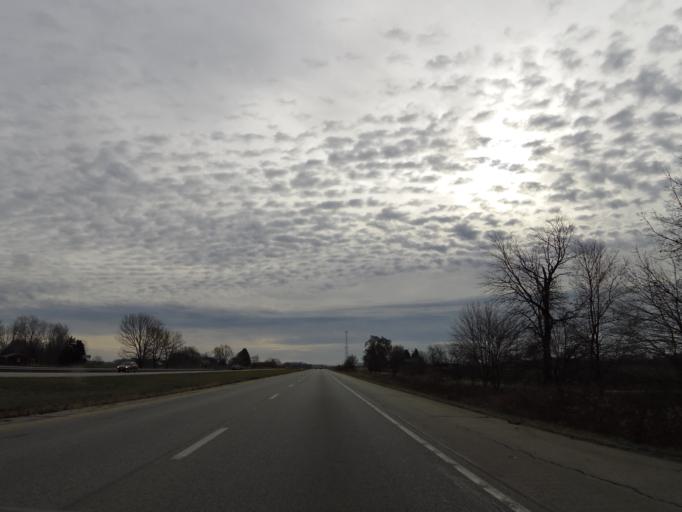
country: US
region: Indiana
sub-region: Hendricks County
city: Pittsboro
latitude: 39.9233
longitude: -86.5845
